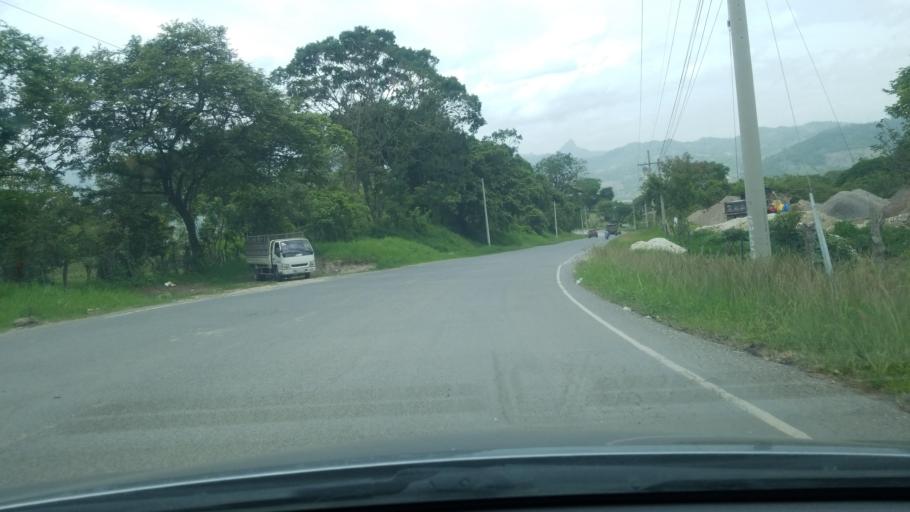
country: HN
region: Copan
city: Santa Rosa de Copan
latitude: 14.7408
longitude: -88.7740
